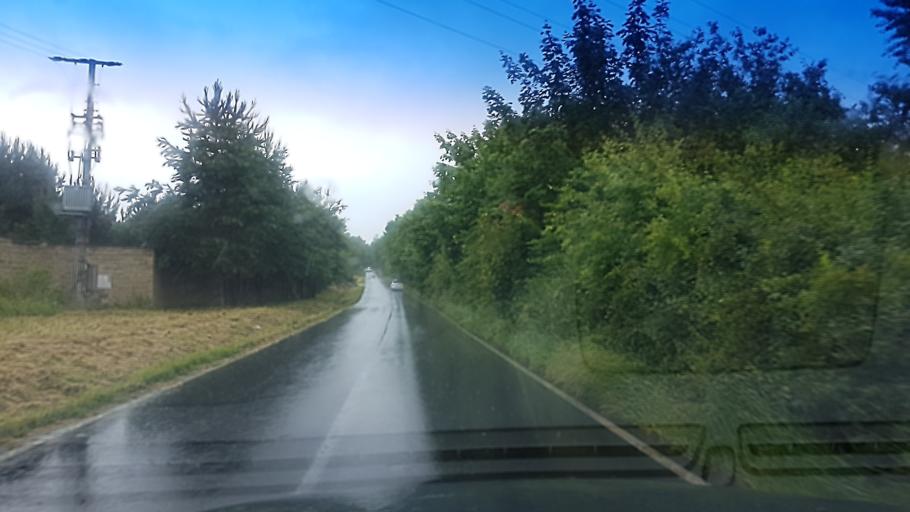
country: CZ
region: Karlovarsky
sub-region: Okres Cheb
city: Cheb
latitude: 50.0640
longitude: 12.3661
